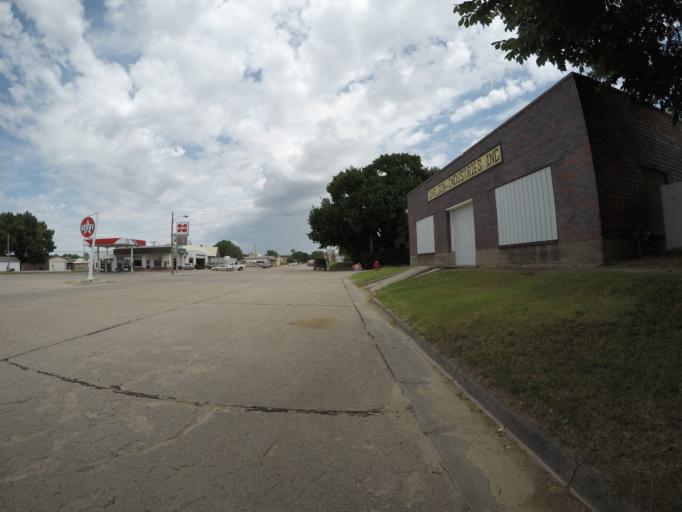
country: US
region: Kansas
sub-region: Rawlins County
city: Atwood
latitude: 39.8065
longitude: -101.0451
